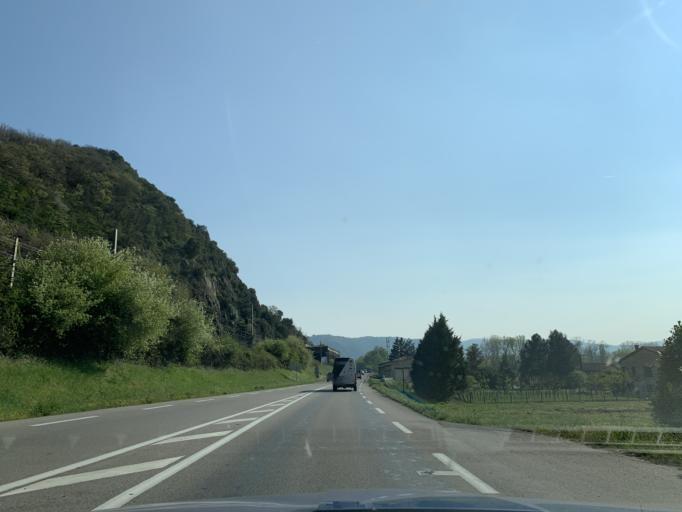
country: FR
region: Rhone-Alpes
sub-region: Departement de l'Ardeche
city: Saint-Jean-de-Muzols
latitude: 45.0941
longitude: 4.8356
